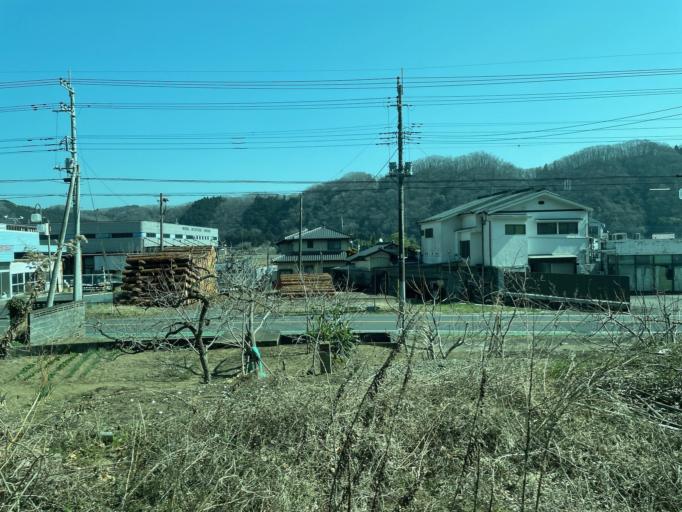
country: JP
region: Ibaraki
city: Omiya
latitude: 36.6271
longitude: 140.4002
